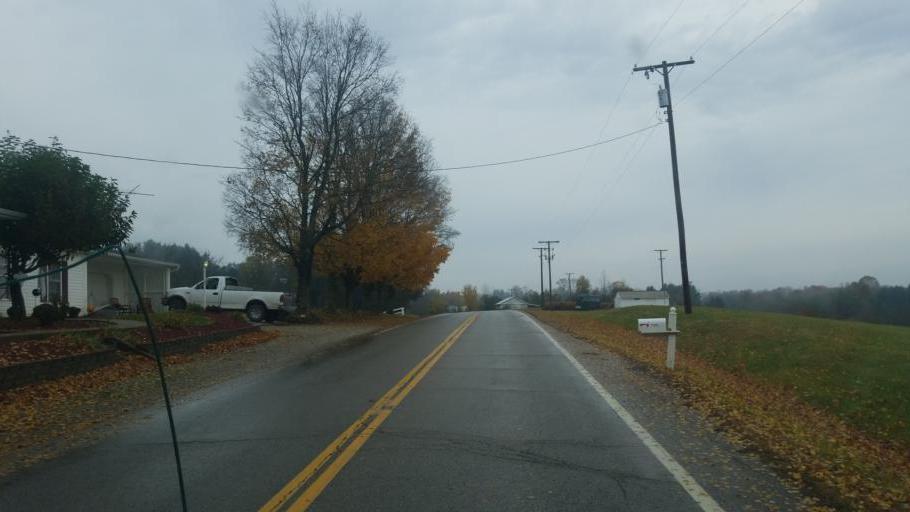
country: US
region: Ohio
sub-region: Morgan County
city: McConnelsville
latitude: 39.4819
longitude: -81.8692
